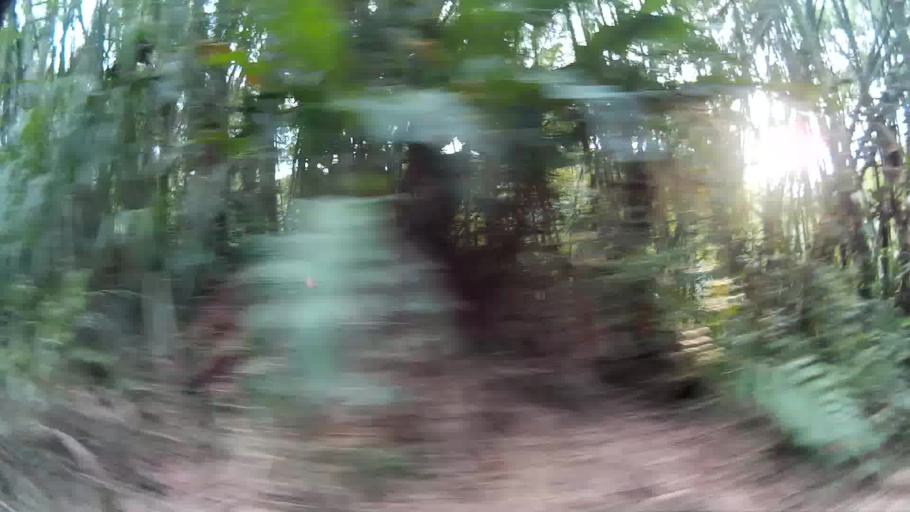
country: CO
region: Valle del Cauca
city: Ulloa
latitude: 4.7373
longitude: -75.7417
